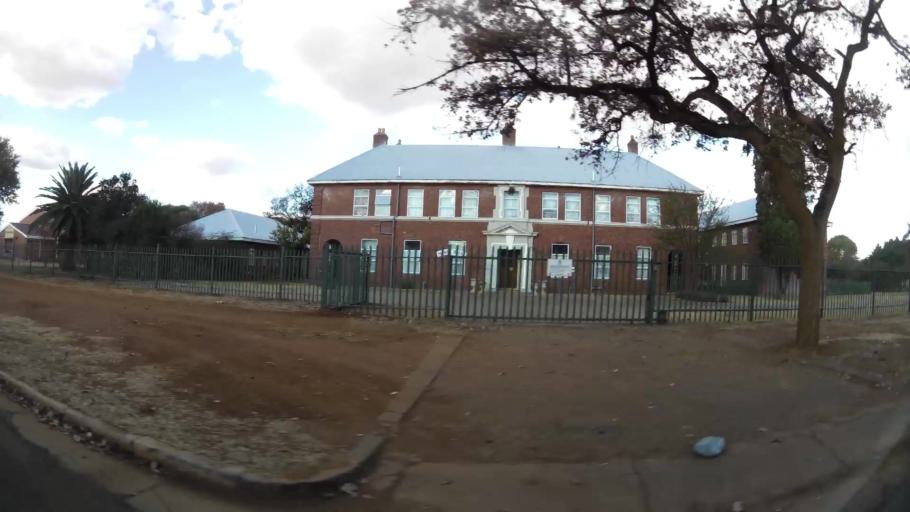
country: ZA
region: North-West
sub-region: Dr Kenneth Kaunda District Municipality
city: Potchefstroom
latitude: -26.7198
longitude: 27.0886
